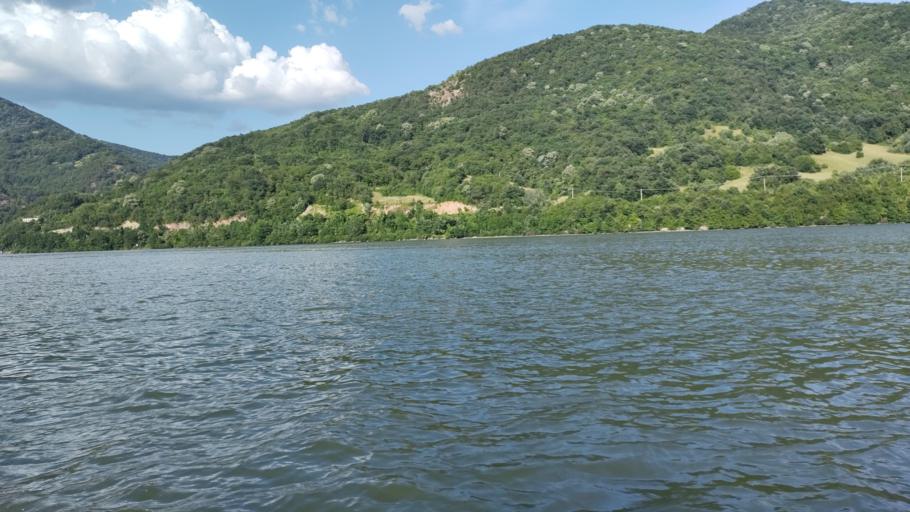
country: RO
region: Caras-Severin
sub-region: Comuna Berzasca
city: Berzasca
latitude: 44.5751
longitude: 22.0273
